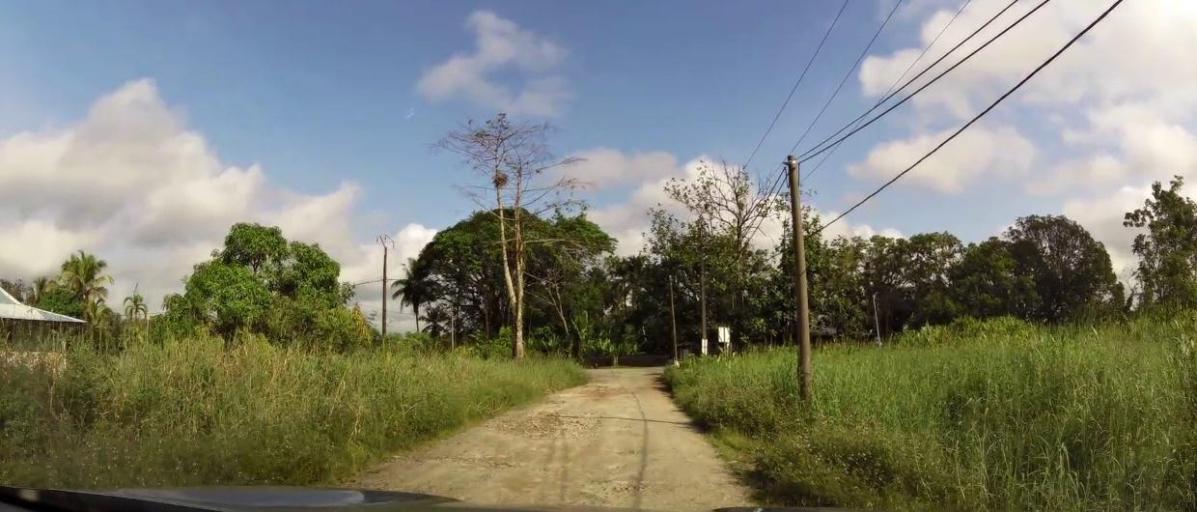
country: GF
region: Guyane
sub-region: Guyane
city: Roura
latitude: 4.7853
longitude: -52.3369
